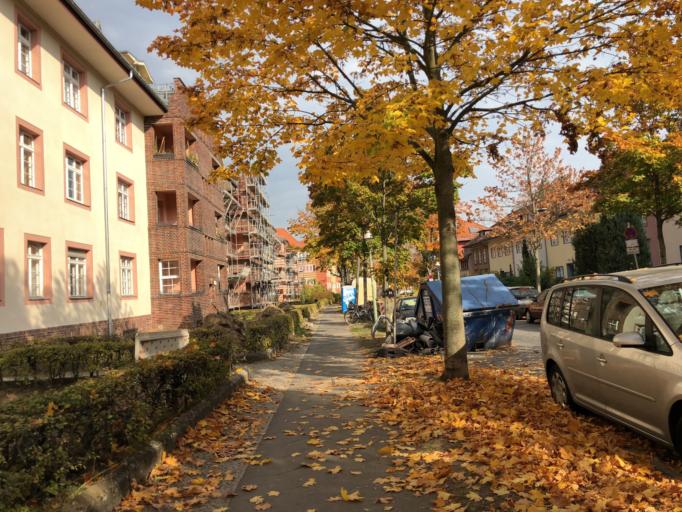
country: DE
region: Berlin
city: Lichterfelde
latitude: 52.4493
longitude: 13.3087
